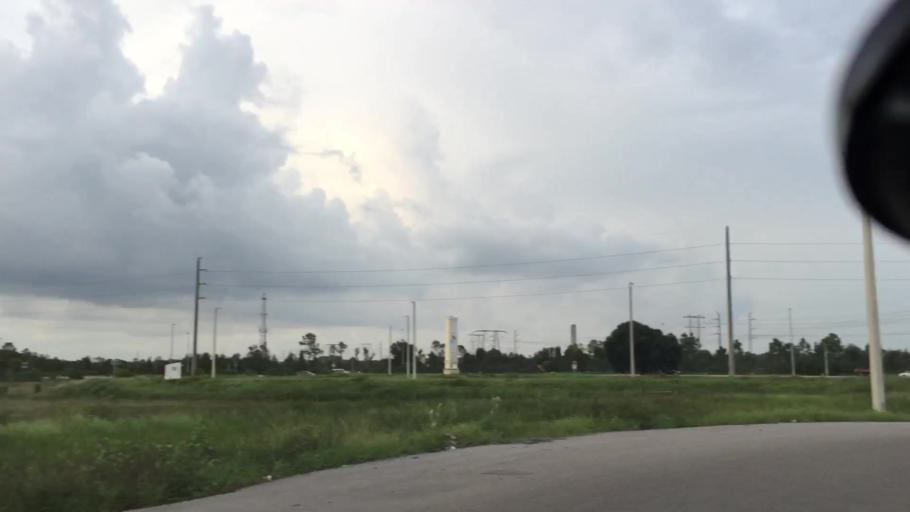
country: US
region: Florida
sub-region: Lee County
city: Gateway
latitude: 26.6183
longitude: -81.7704
